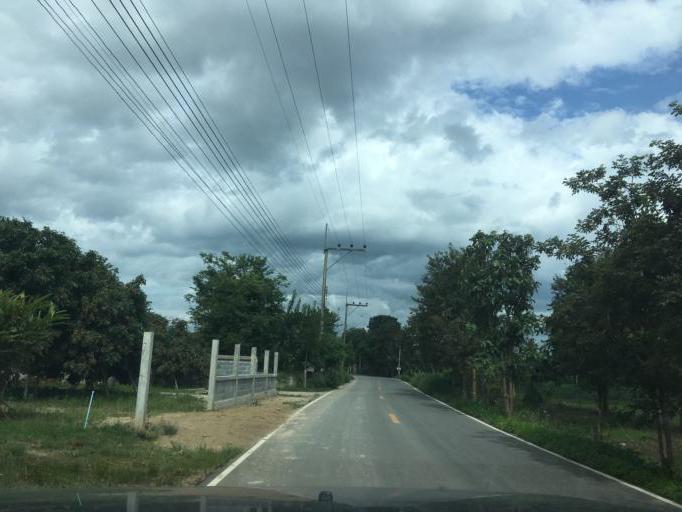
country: TH
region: Chiang Rai
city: Wiang Pa Pao
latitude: 19.2339
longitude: 99.4919
